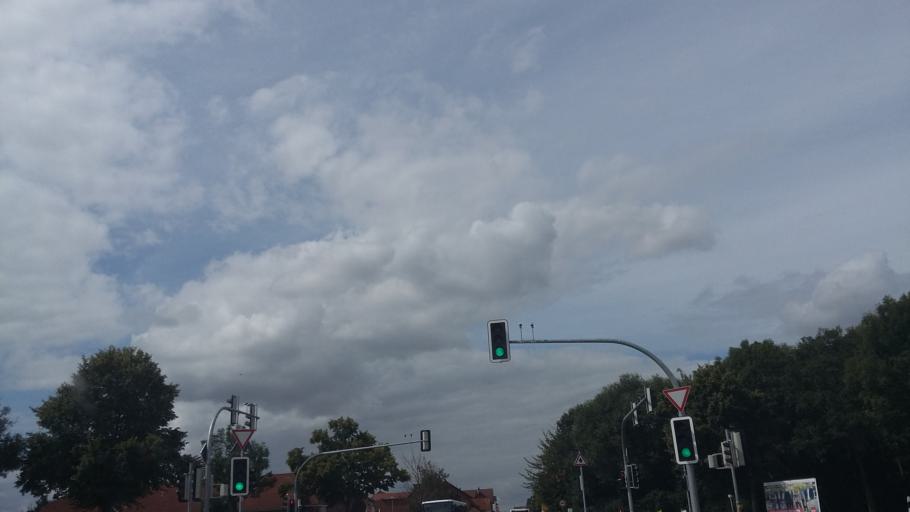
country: DE
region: Lower Saxony
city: Harsum
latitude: 52.2072
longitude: 9.9730
